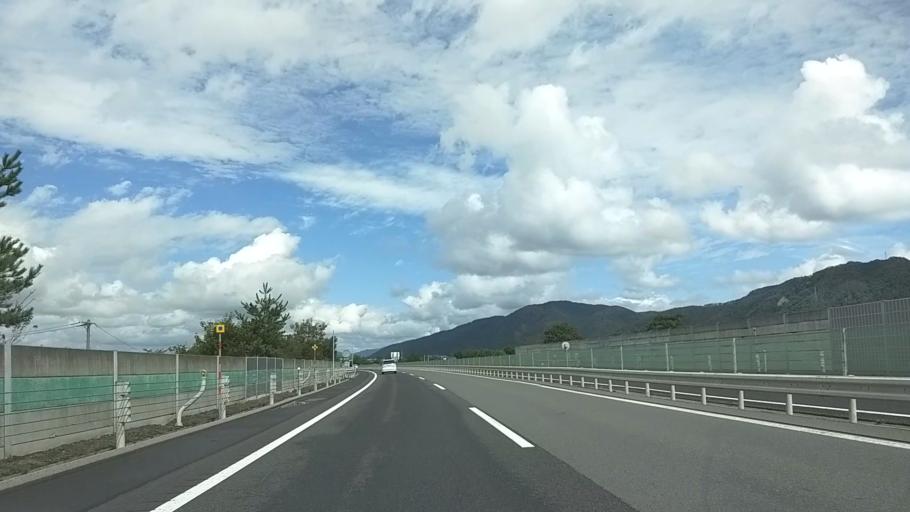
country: JP
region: Nagano
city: Toyoshina
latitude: 36.2784
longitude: 137.9313
